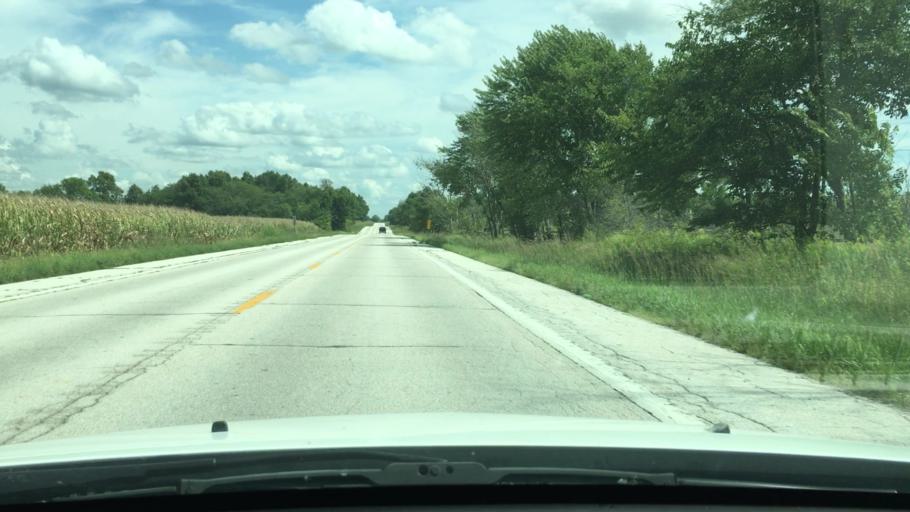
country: US
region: Missouri
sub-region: Audrain County
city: Vandalia
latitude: 39.3244
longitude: -91.4528
